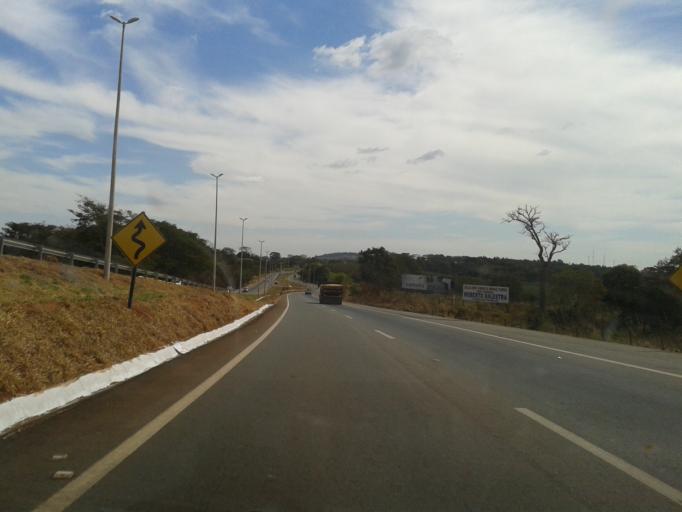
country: BR
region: Goias
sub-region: Inhumas
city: Inhumas
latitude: -16.4044
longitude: -49.4817
